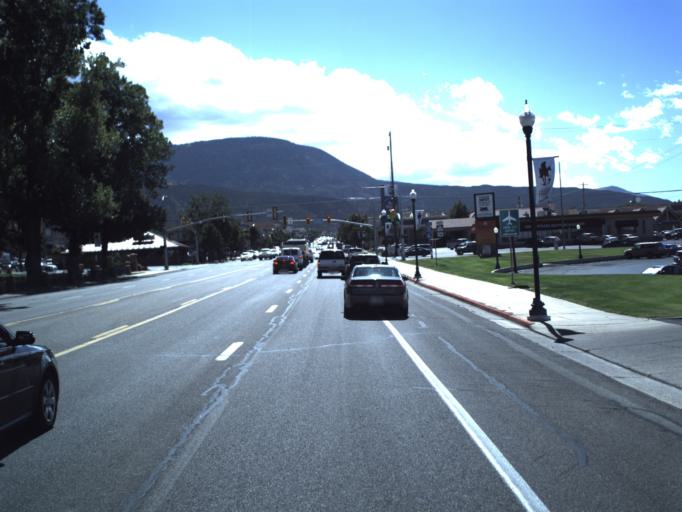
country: US
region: Utah
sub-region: Iron County
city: Cedar City
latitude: 37.6821
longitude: -113.0619
